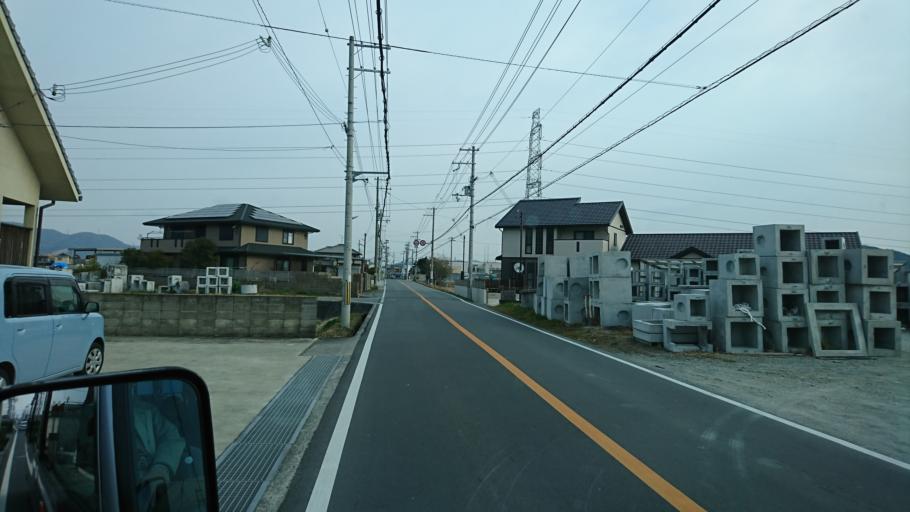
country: JP
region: Hyogo
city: Kakogawacho-honmachi
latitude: 34.8017
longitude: 134.8165
